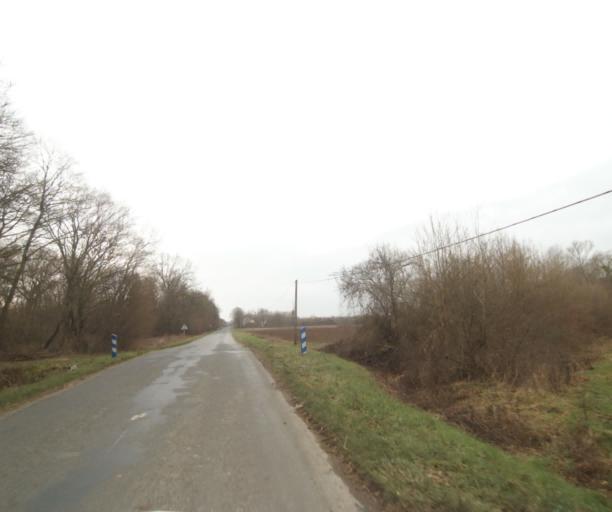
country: FR
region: Champagne-Ardenne
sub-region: Departement de la Haute-Marne
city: Villiers-en-Lieu
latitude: 48.6572
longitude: 4.8780
